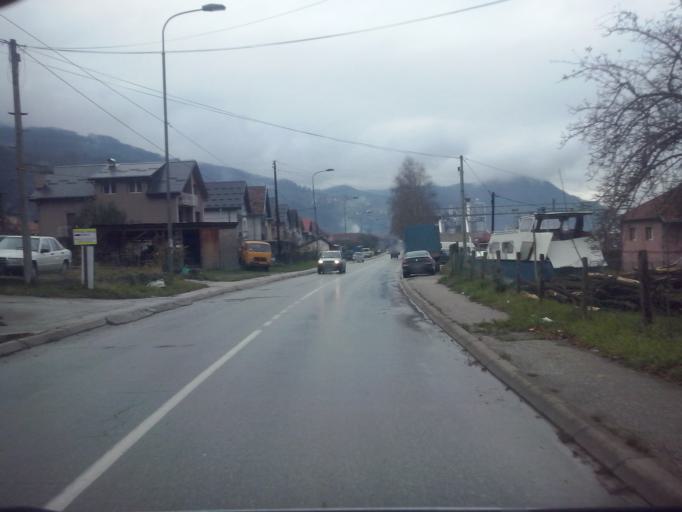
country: RS
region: Central Serbia
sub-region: Moravicki Okrug
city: Ivanjica
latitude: 43.5661
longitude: 20.2476
